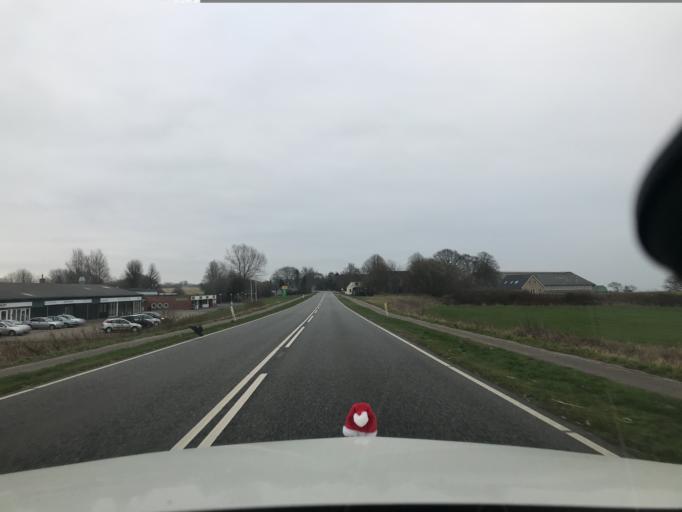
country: DK
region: South Denmark
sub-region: Sonderborg Kommune
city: Dybbol
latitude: 54.9104
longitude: 9.7120
